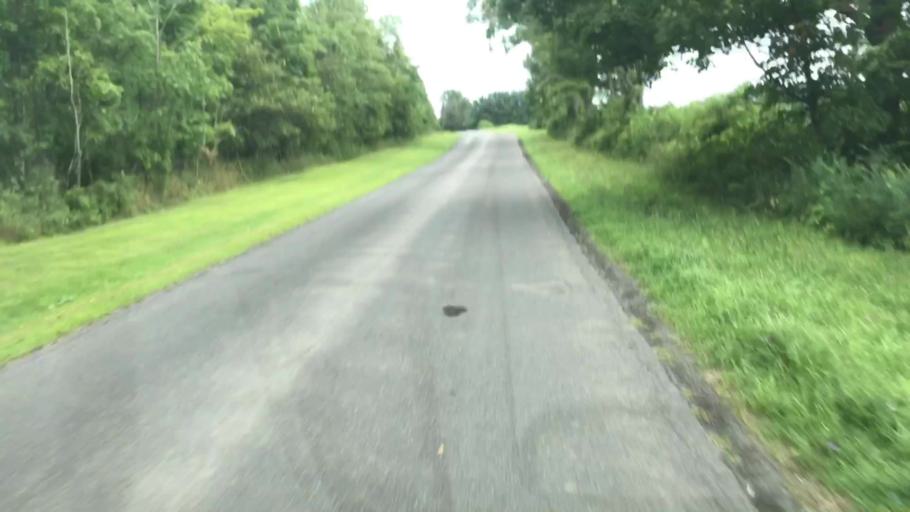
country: US
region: New York
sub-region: Onondaga County
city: Elbridge
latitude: 42.9996
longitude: -76.4451
